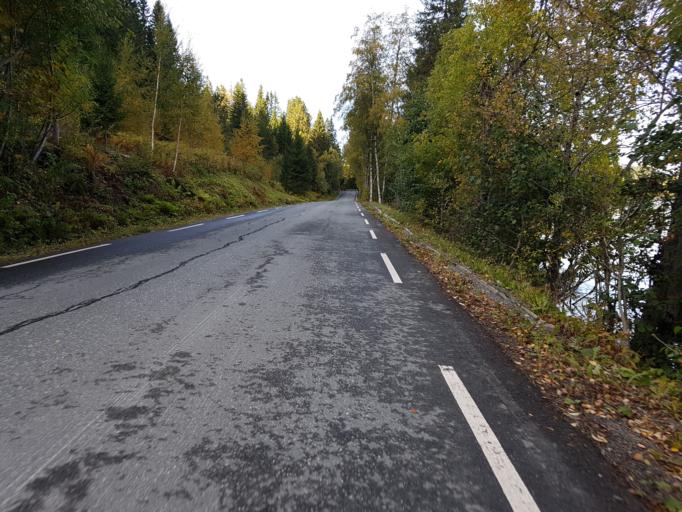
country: NO
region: Sor-Trondelag
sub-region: Klaebu
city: Klaebu
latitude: 63.3404
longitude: 10.5596
